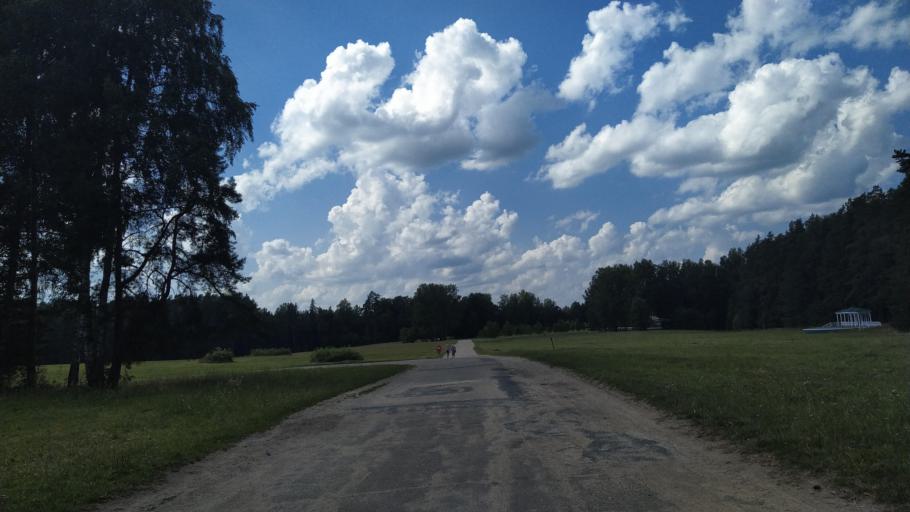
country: RU
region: Pskov
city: Pushkinskiye Gory
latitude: 57.0595
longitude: 28.9306
